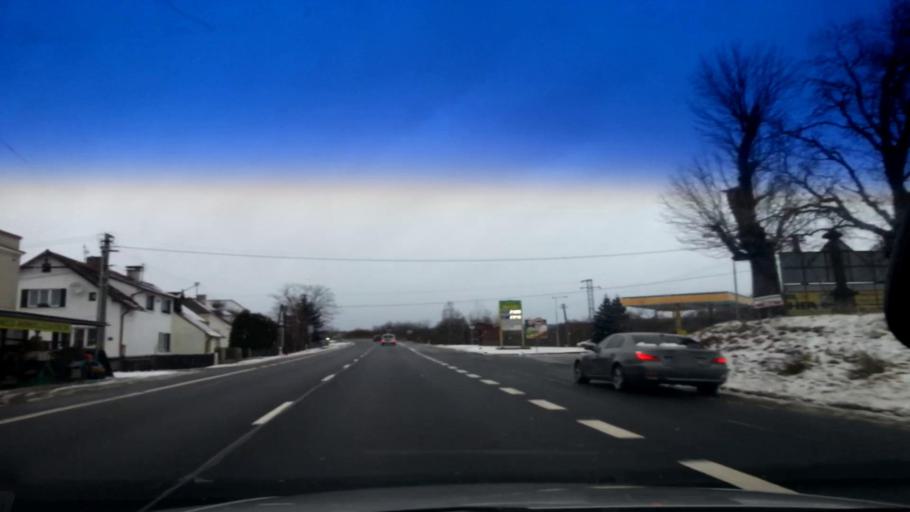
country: CZ
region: Karlovarsky
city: Hazlov
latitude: 50.1615
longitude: 12.2704
